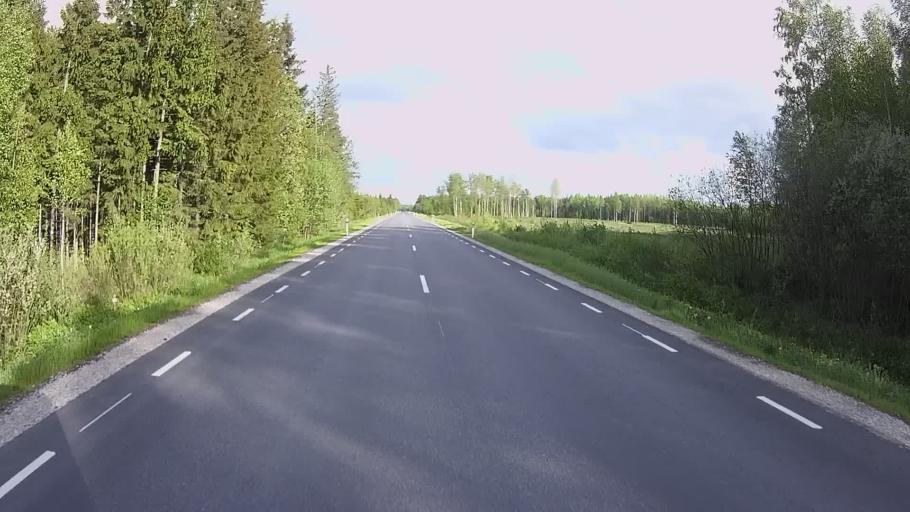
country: EE
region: Ida-Virumaa
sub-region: Kivioli linn
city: Kivioli
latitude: 59.2074
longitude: 26.8065
